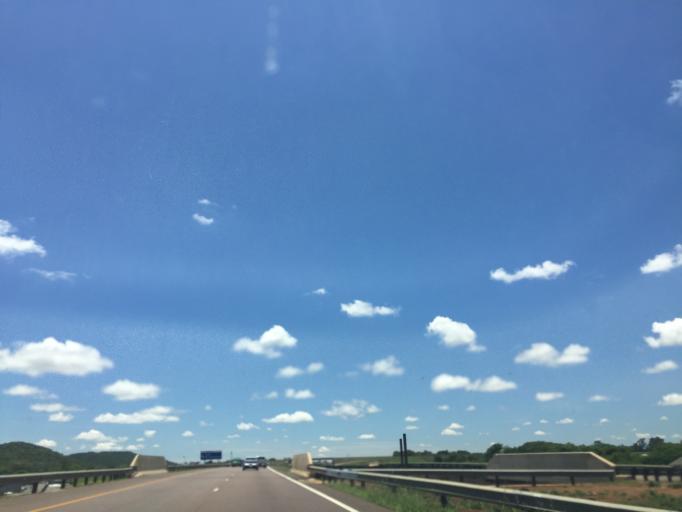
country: ZA
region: Gauteng
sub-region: City of Tshwane Metropolitan Municipality
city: Pretoria
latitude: -25.6378
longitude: 28.1968
